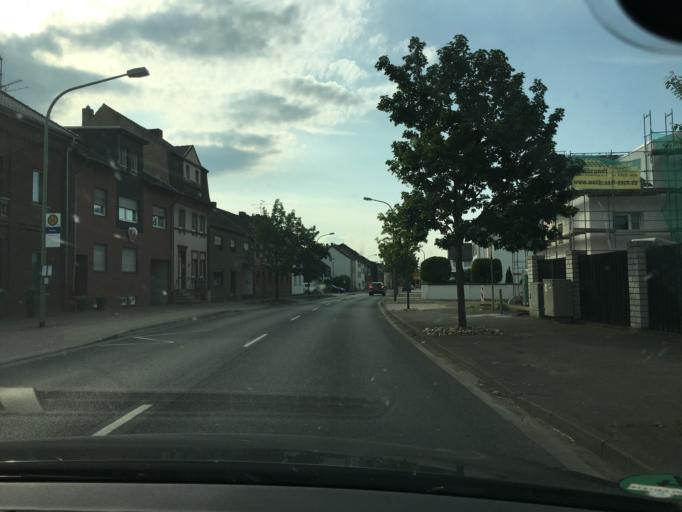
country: DE
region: North Rhine-Westphalia
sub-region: Regierungsbezirk Koln
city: Kreuzau
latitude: 50.7438
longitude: 6.4959
